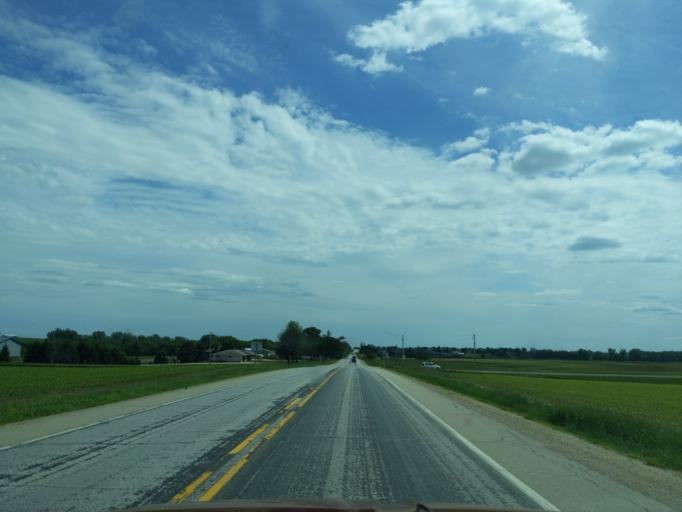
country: US
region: Wisconsin
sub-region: Dane County
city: De Forest
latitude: 43.2823
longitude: -89.3248
